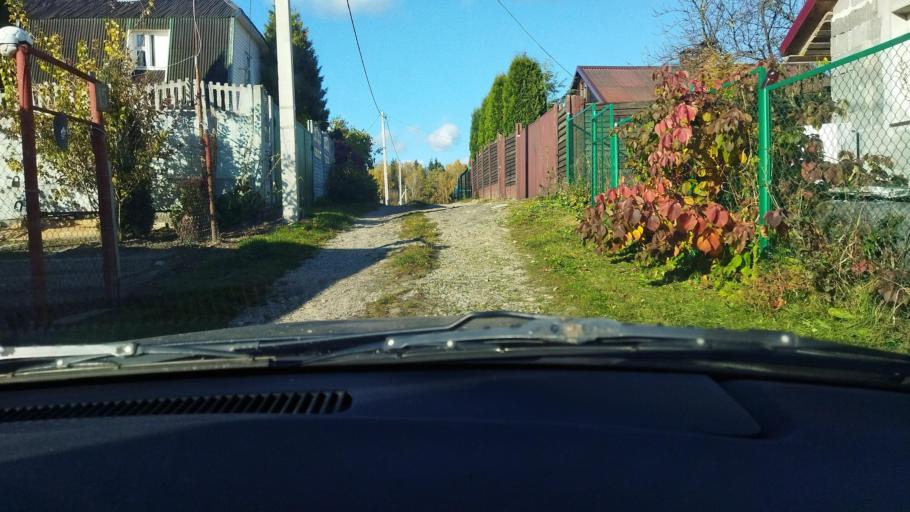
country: BY
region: Minsk
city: Slabada
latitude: 53.9894
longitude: 27.8912
